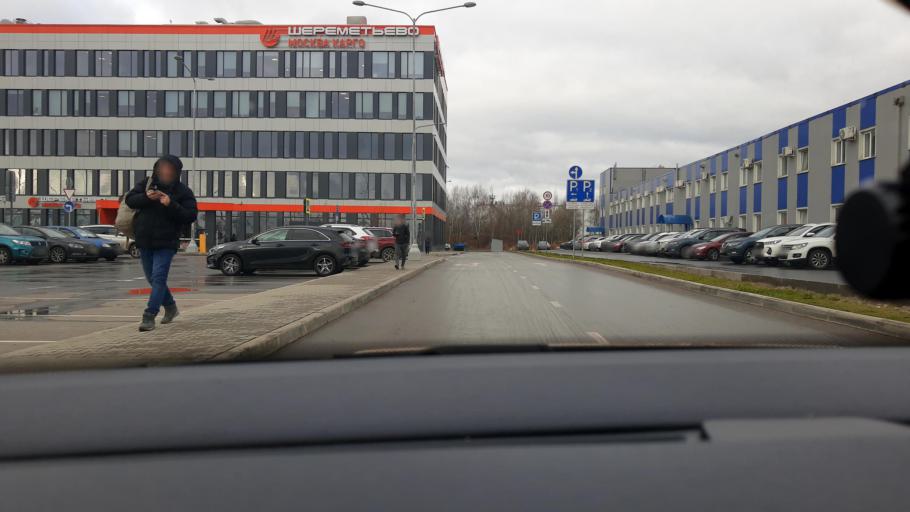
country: RU
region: Moskovskaya
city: Lobnya
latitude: 55.9848
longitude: 37.4291
